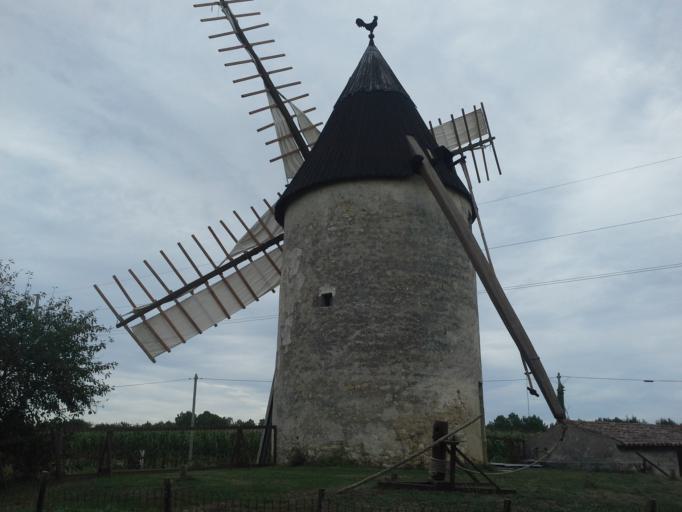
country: FR
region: Aquitaine
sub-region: Departement de la Gironde
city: Gaillan-en-Medoc
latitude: 45.3992
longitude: -1.0518
